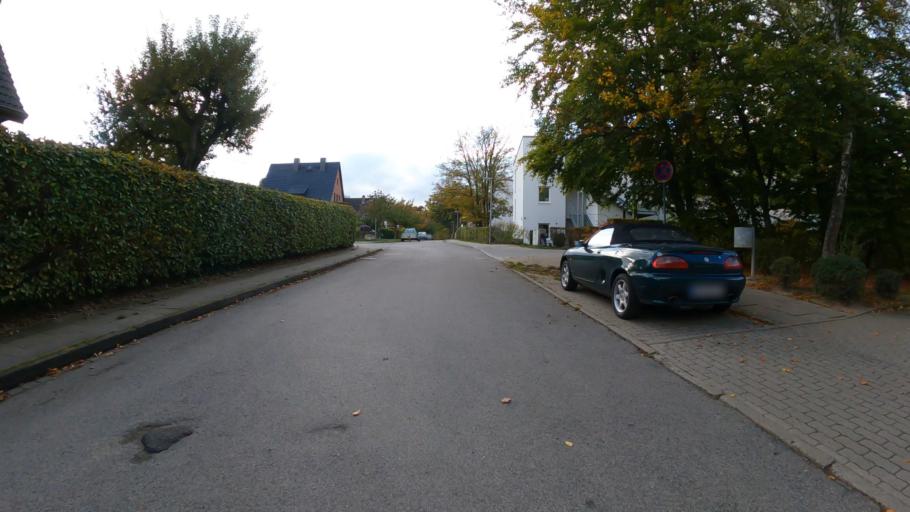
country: DE
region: Schleswig-Holstein
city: Ahrensburg
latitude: 53.6748
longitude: 10.2484
